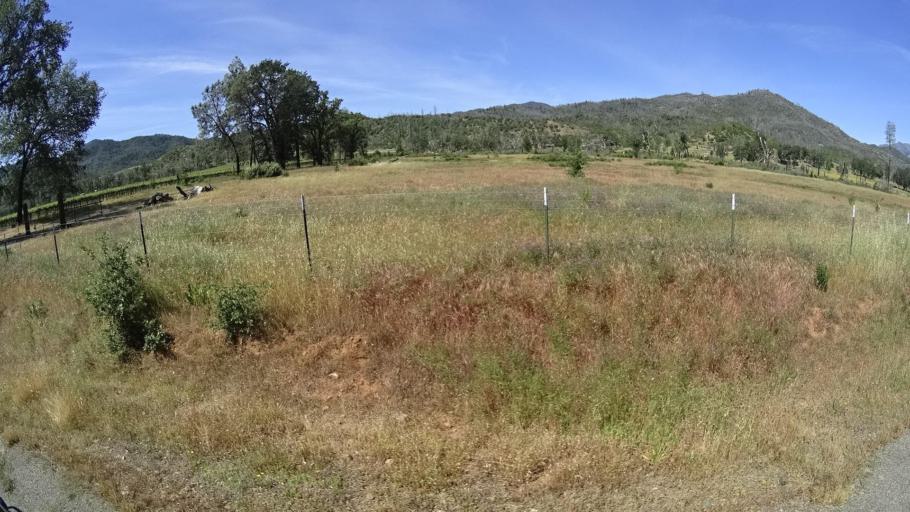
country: US
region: California
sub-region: Lake County
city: Middletown
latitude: 38.7503
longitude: -122.6357
